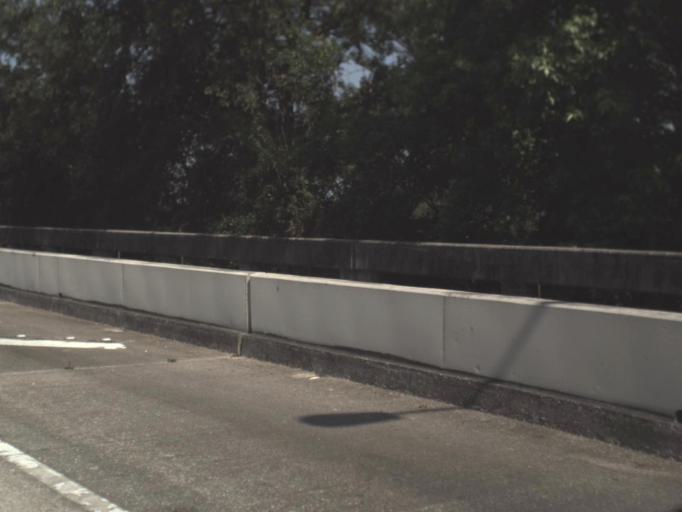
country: US
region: Florida
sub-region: Clay County
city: Bellair-Meadowbrook Terrace
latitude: 30.2476
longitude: -81.7074
